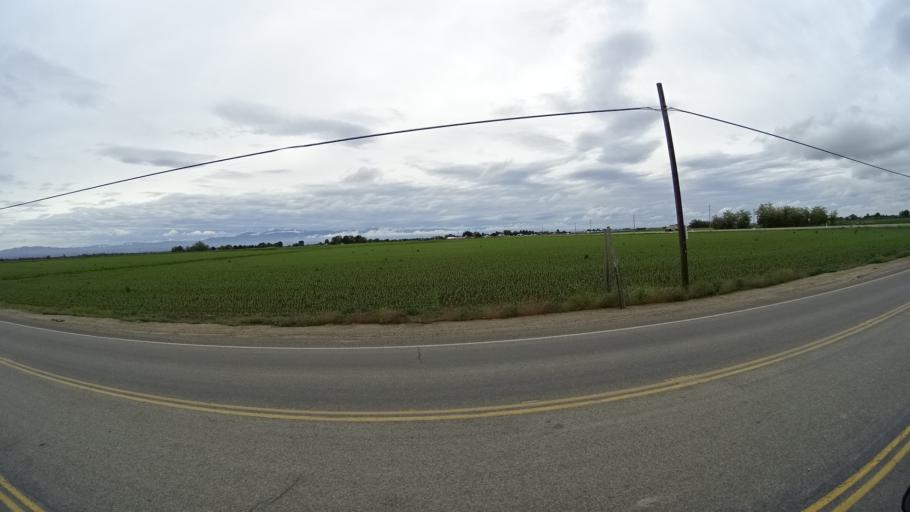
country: US
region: Idaho
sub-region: Ada County
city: Star
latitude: 43.6643
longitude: -116.4935
